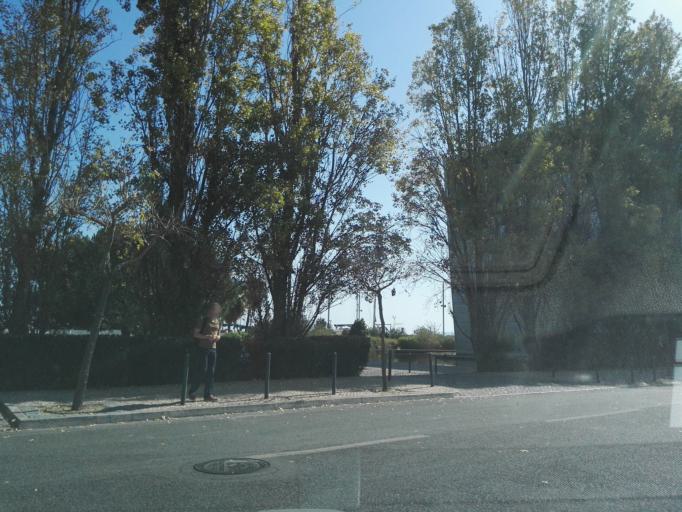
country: PT
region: Lisbon
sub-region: Loures
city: Moscavide
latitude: 38.7542
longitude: -9.0951
